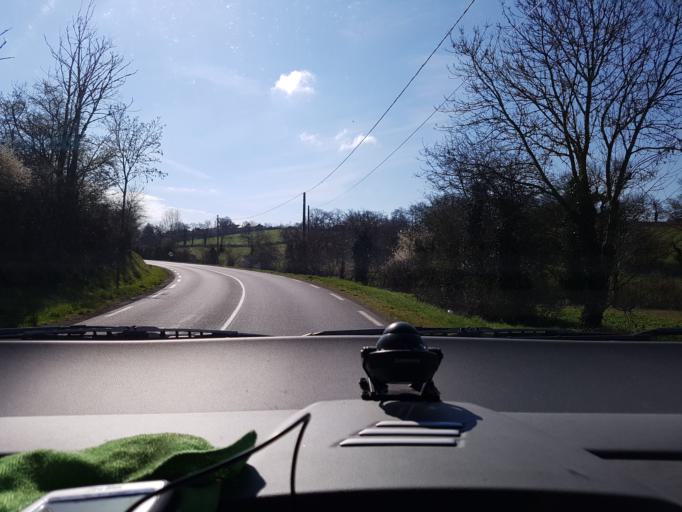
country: FR
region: Midi-Pyrenees
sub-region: Departement de l'Aveyron
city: Olemps
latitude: 44.3670
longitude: 2.5418
